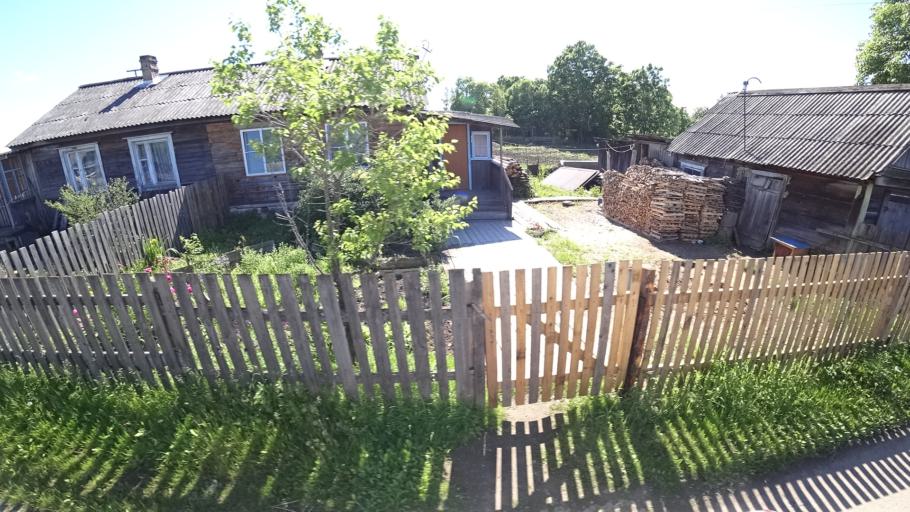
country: RU
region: Khabarovsk Krai
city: Khor
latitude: 47.8862
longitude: 135.0368
